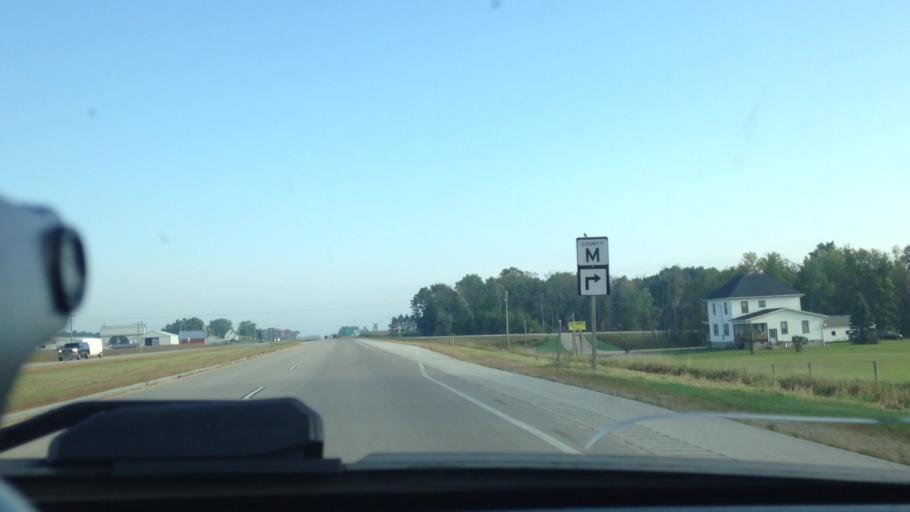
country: US
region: Wisconsin
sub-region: Oconto County
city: Oconto Falls
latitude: 45.0343
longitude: -88.0445
